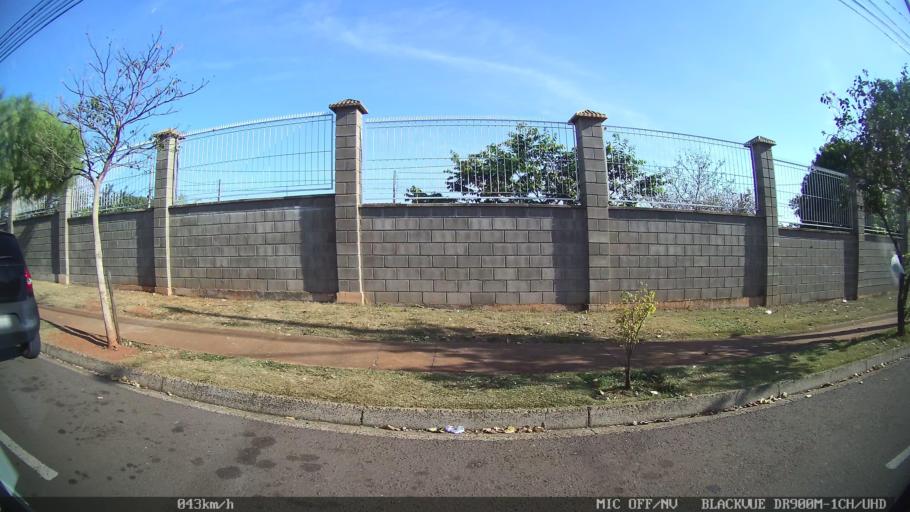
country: BR
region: Sao Paulo
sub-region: Sao Jose Do Rio Preto
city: Sao Jose do Rio Preto
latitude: -20.7719
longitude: -49.3324
